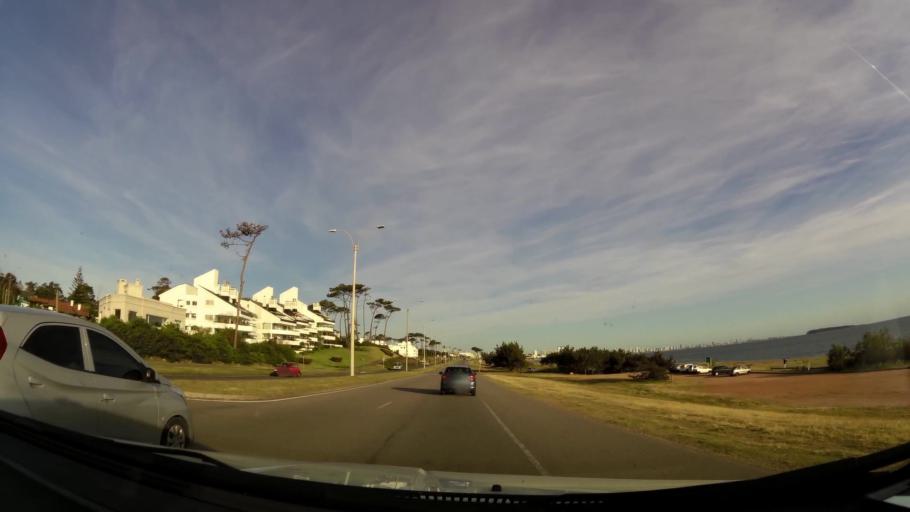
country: UY
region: Maldonado
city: Maldonado
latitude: -34.9112
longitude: -54.9931
